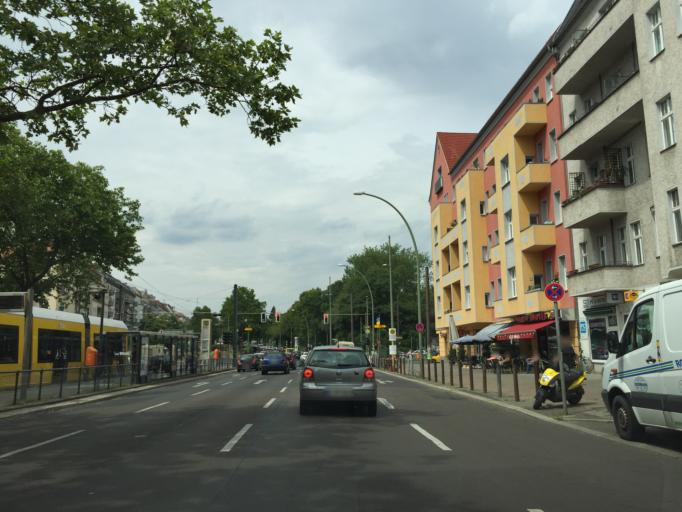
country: DE
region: Berlin
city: Prenzlauer Berg Bezirk
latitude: 52.5358
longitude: 13.4343
